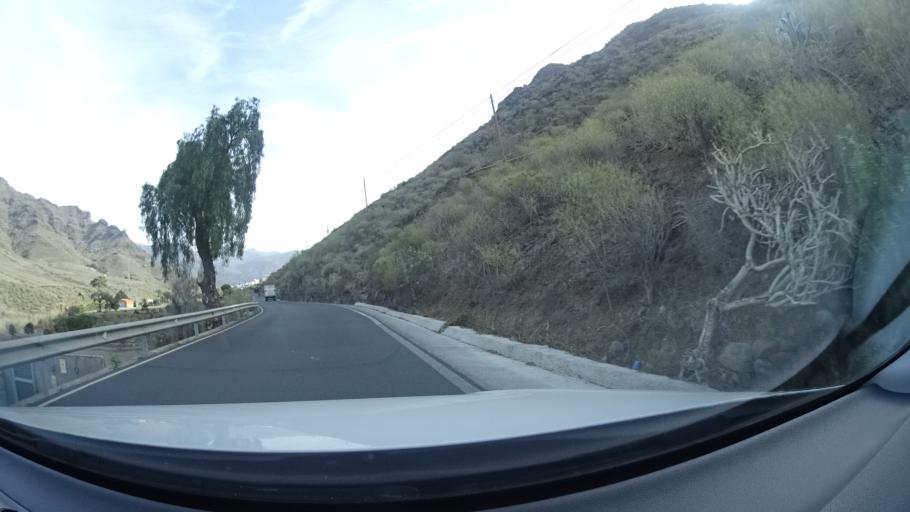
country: ES
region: Canary Islands
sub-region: Provincia de Las Palmas
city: Mogan
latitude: 27.8679
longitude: -15.7399
